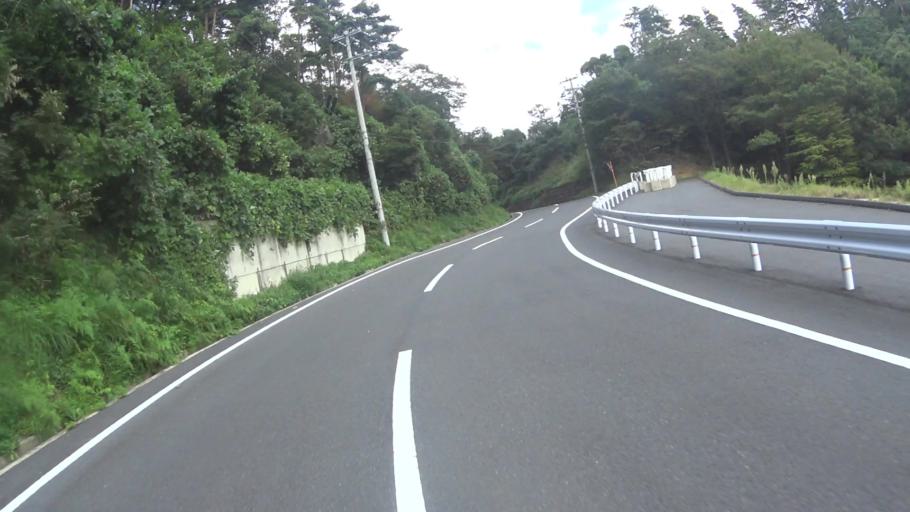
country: JP
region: Kyoto
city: Miyazu
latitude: 35.7328
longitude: 135.1782
